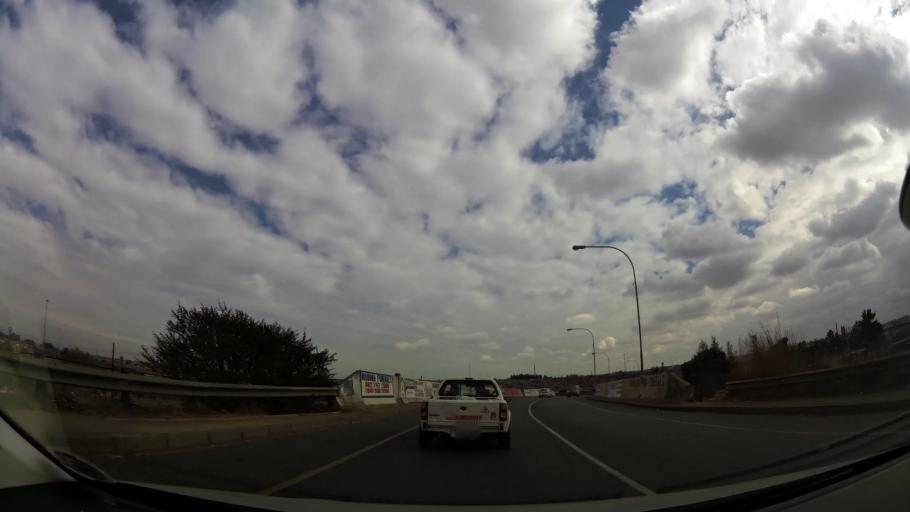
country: ZA
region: Gauteng
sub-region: City of Johannesburg Metropolitan Municipality
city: Soweto
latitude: -26.2746
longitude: 27.8880
